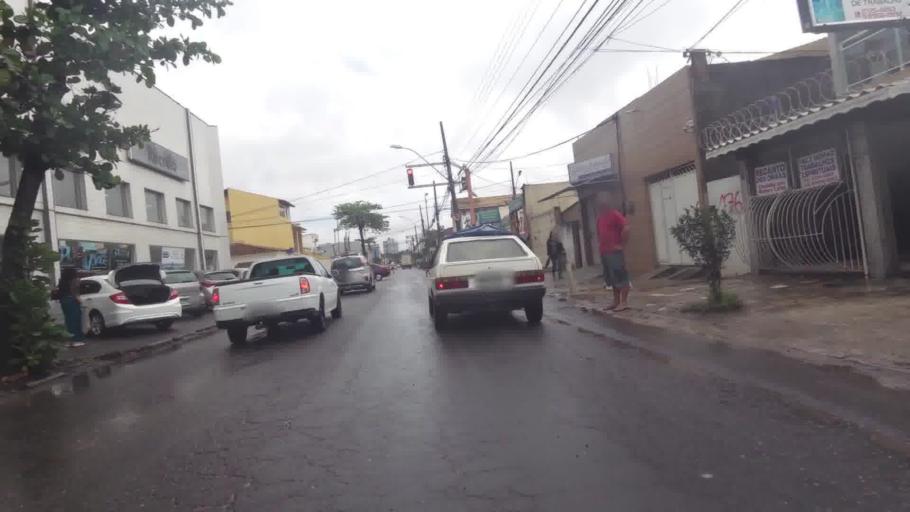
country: BR
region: Rio de Janeiro
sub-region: Campos Dos Goytacazes
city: Campos
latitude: -21.7448
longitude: -41.3351
